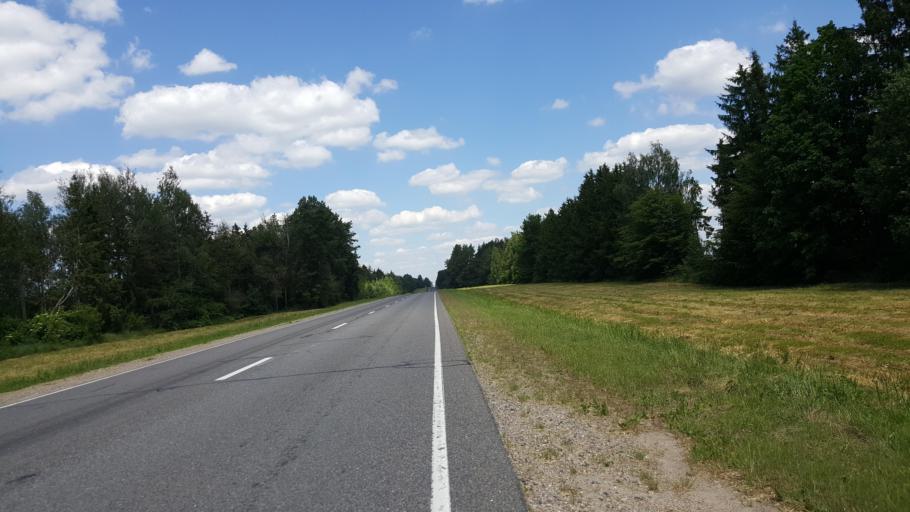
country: BY
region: Brest
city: Kamyanyets
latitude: 52.4488
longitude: 23.7837
